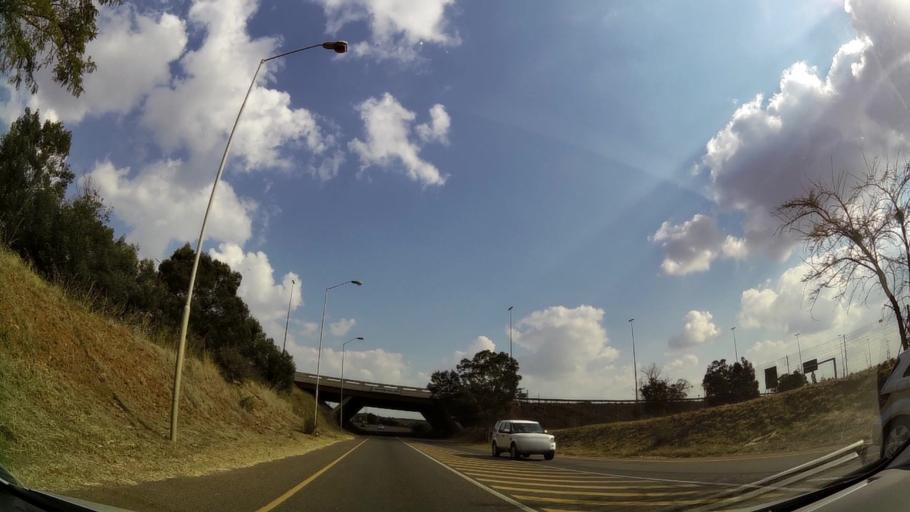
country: ZA
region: Gauteng
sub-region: City of Tshwane Metropolitan Municipality
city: Centurion
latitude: -25.8192
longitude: 28.2391
